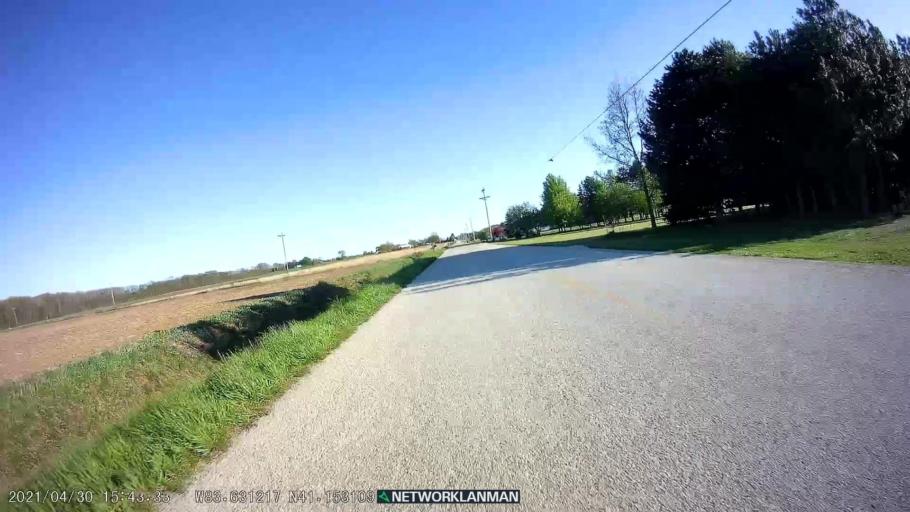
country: US
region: Ohio
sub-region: Wood County
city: North Baltimore
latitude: 41.1535
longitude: -83.6312
